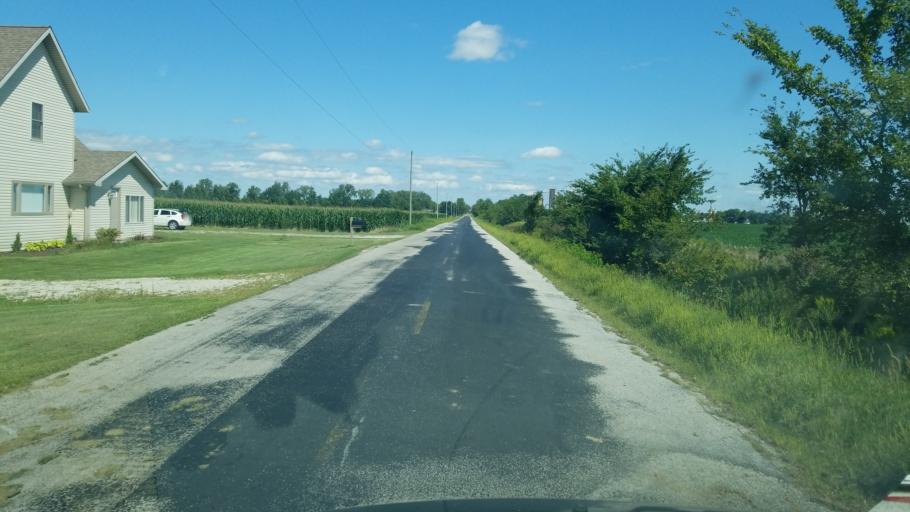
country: US
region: Ohio
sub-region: Wood County
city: Weston
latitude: 41.2737
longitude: -83.8439
